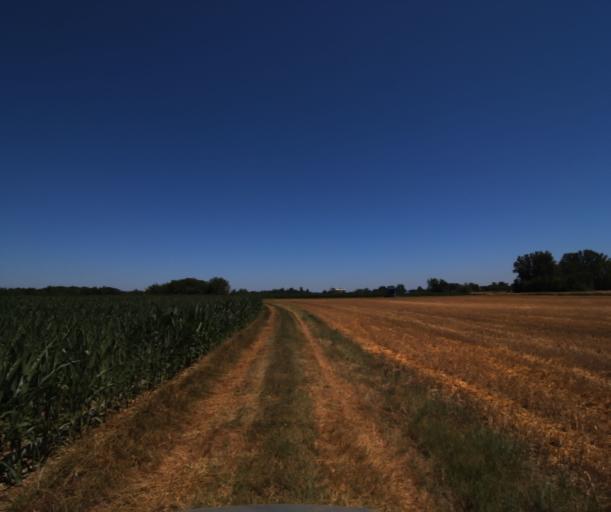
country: FR
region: Midi-Pyrenees
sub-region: Departement de la Haute-Garonne
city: Seysses
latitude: 43.4670
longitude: 1.2913
